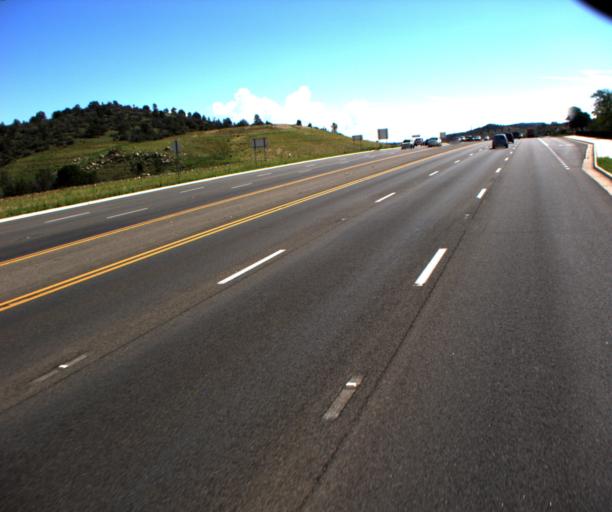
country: US
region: Arizona
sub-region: Yavapai County
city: Prescott
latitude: 34.5488
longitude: -112.4421
